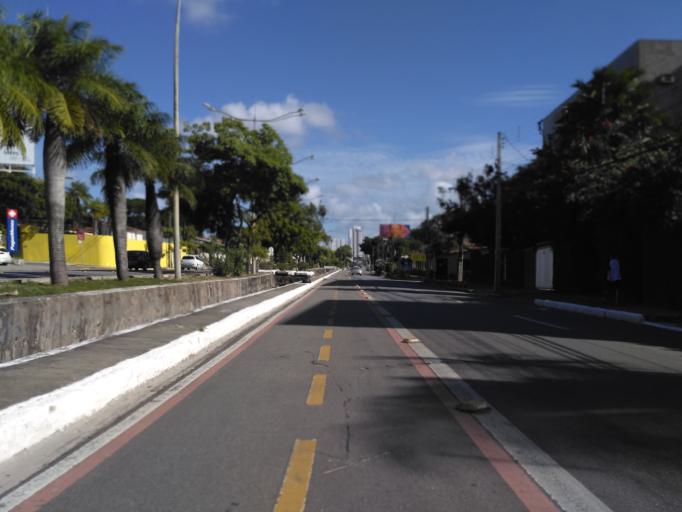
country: BR
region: Pernambuco
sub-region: Jaboatao Dos Guararapes
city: Jaboatao
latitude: -8.1612
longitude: -34.9141
